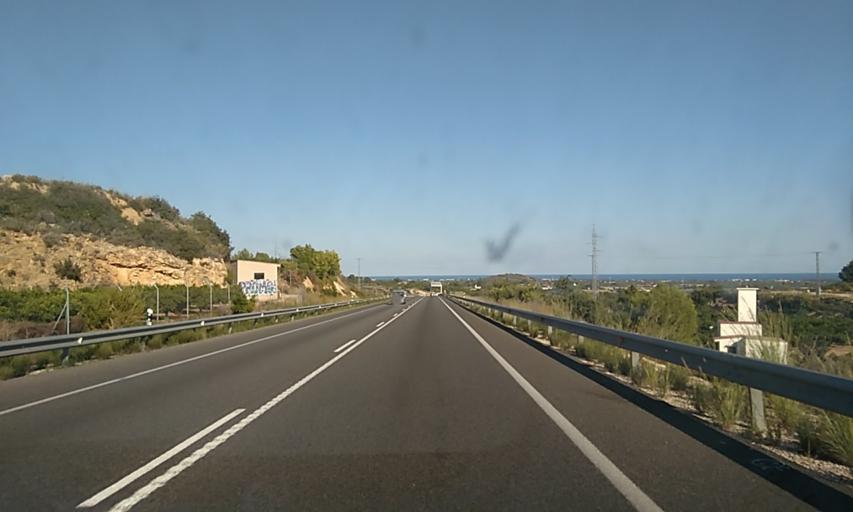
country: ES
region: Valencia
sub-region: Provincia de Castello
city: Torreblanca
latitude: 40.2308
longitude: 0.1954
